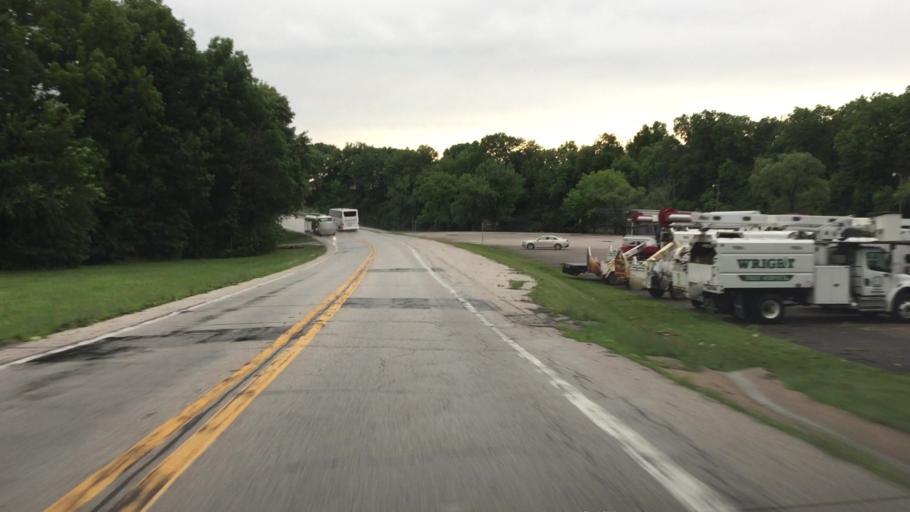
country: US
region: Illinois
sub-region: Hancock County
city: Hamilton
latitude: 40.4059
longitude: -91.3513
